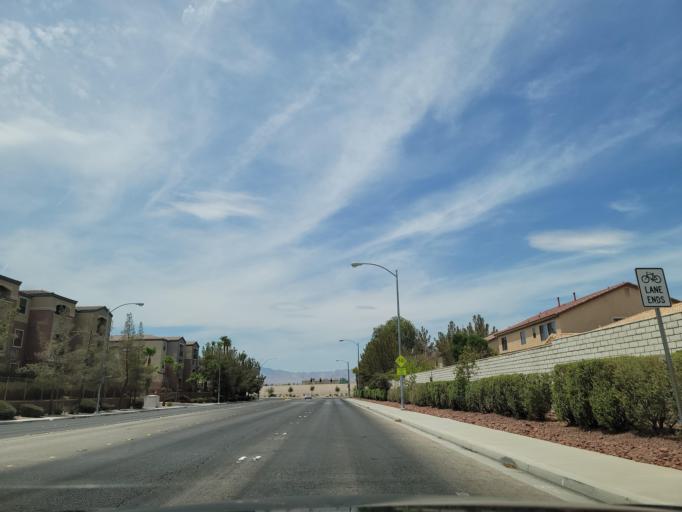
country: US
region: Nevada
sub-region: Clark County
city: Paradise
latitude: 36.0206
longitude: -115.1526
